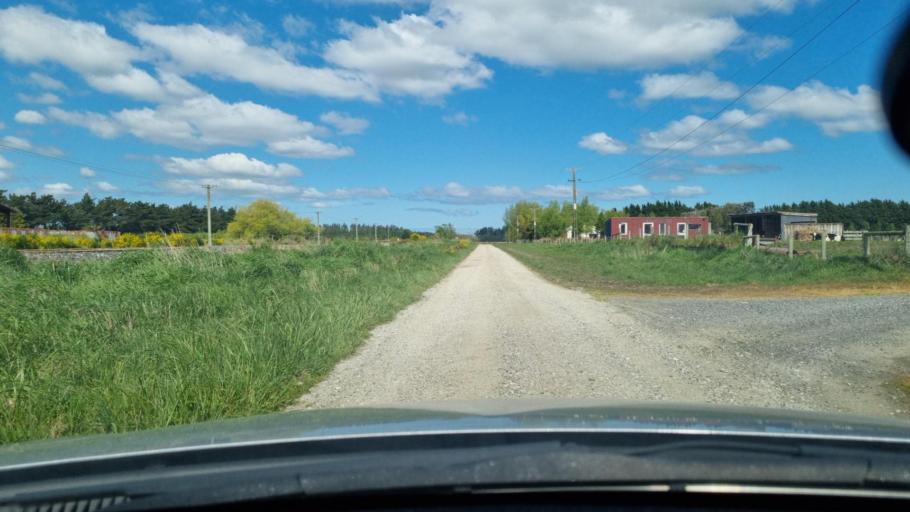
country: NZ
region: Southland
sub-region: Invercargill City
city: Invercargill
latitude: -46.3468
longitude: 168.3401
